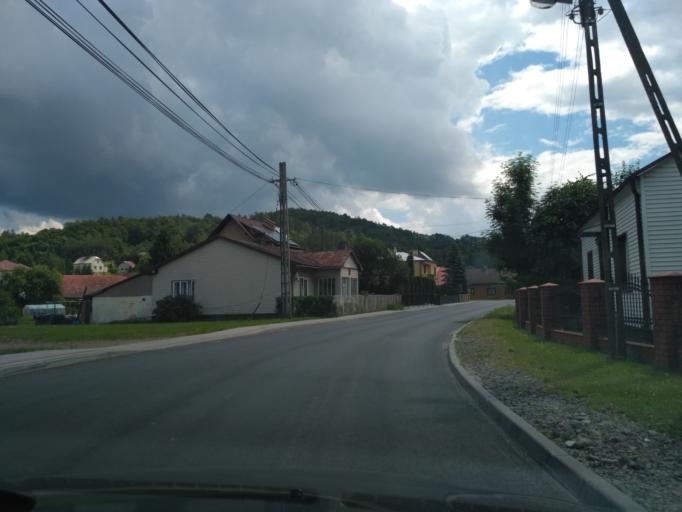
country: PL
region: Subcarpathian Voivodeship
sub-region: Powiat rzeszowski
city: Blazowa
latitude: 49.8802
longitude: 22.0944
